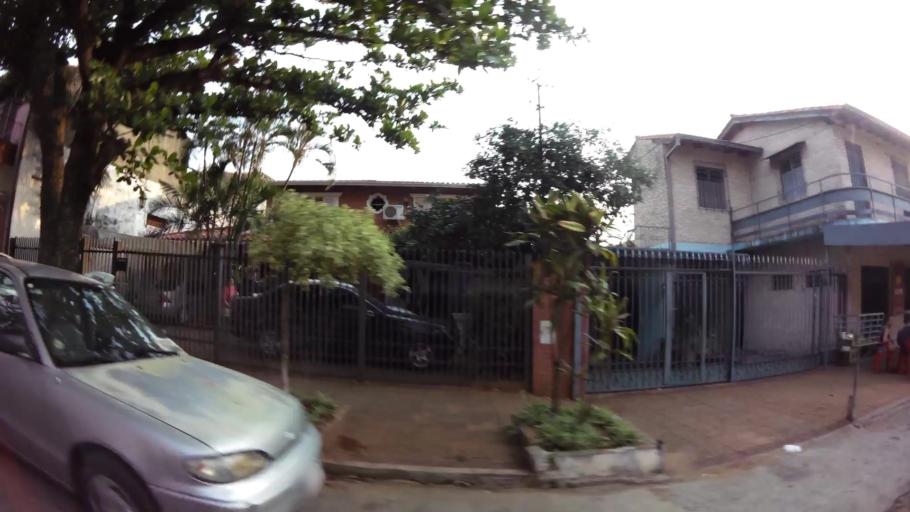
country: PY
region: Central
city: Lambare
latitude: -25.3188
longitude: -57.5767
